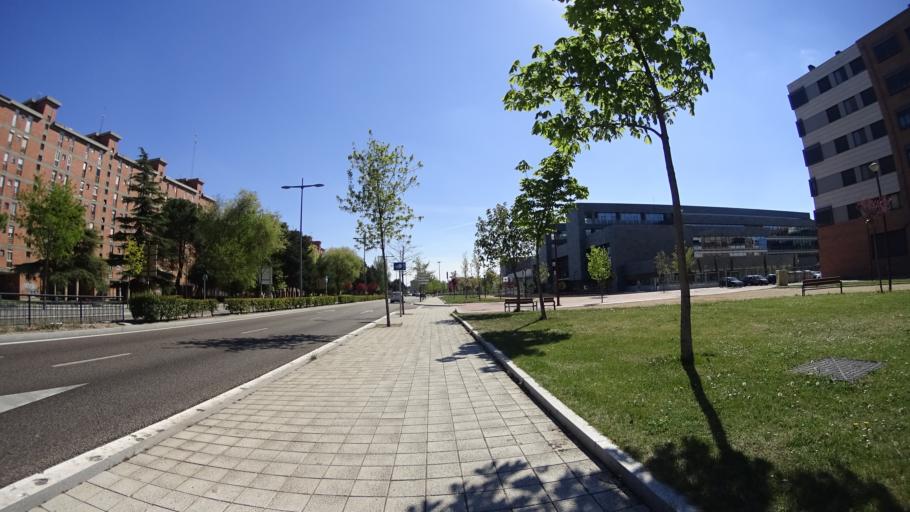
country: ES
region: Castille and Leon
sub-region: Provincia de Valladolid
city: Valladolid
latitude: 41.6463
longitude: -4.7421
